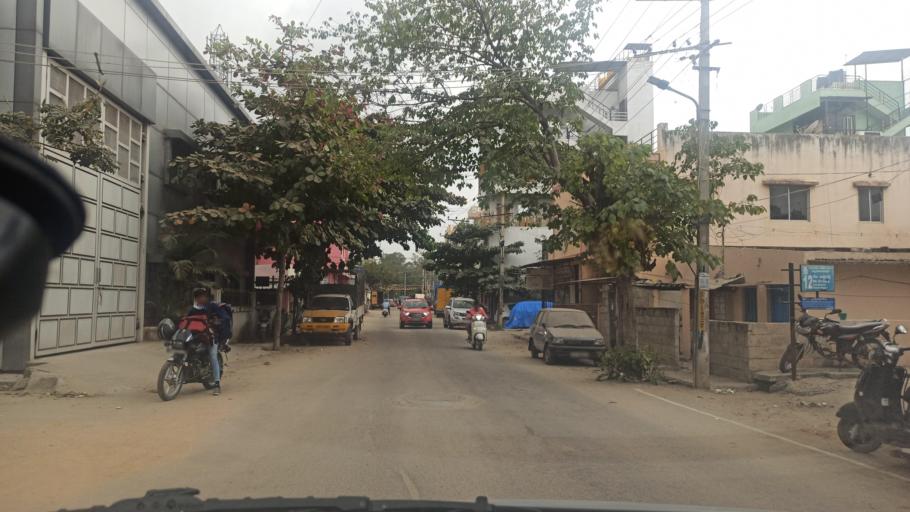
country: IN
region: Karnataka
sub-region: Bangalore Urban
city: Yelahanka
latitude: 13.0455
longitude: 77.6012
